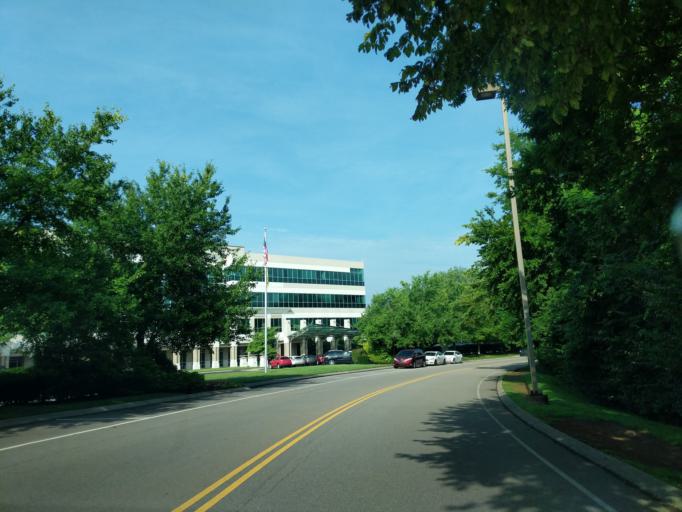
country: US
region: Tennessee
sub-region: Davidson County
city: Goodlettsville
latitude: 36.3098
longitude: -86.6986
